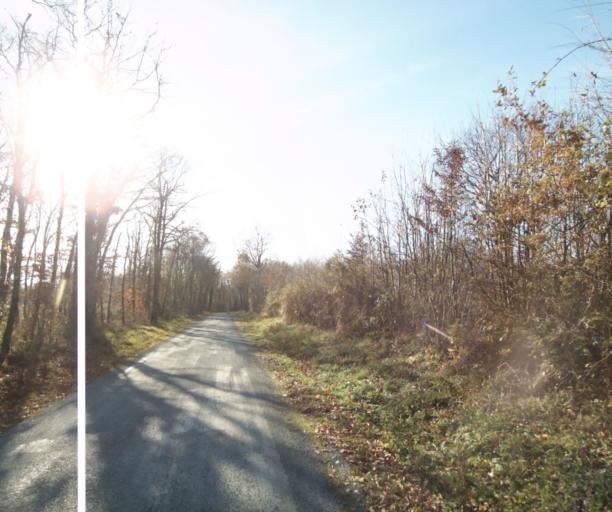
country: FR
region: Poitou-Charentes
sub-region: Departement de la Charente-Maritime
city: Ecoyeux
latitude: 45.7651
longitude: -0.5060
